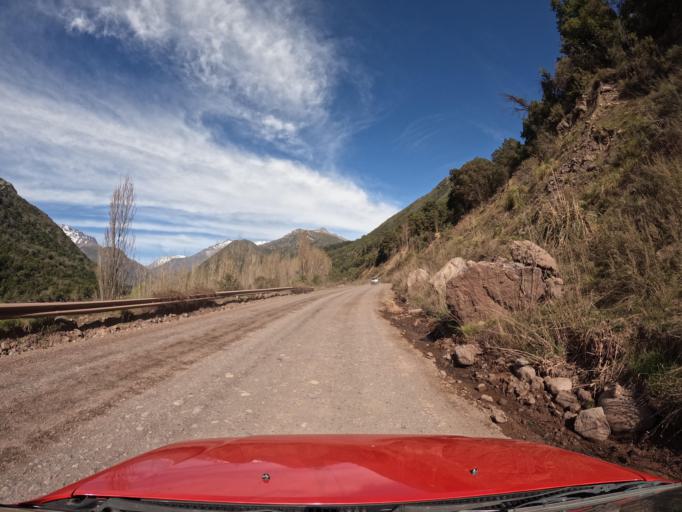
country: CL
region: O'Higgins
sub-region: Provincia de Colchagua
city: Chimbarongo
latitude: -35.0027
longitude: -70.7596
